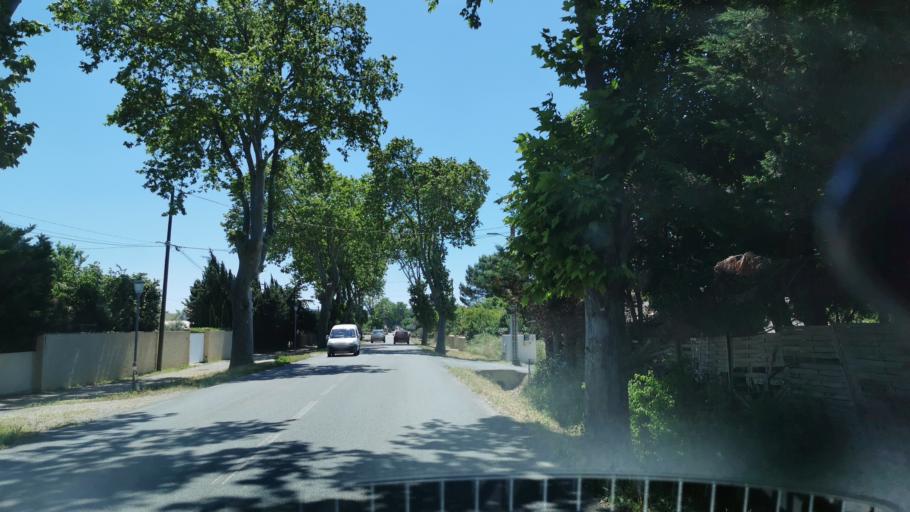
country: FR
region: Languedoc-Roussillon
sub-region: Departement de l'Aude
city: Saint-Marcel-sur-Aude
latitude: 43.2496
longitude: 2.9164
